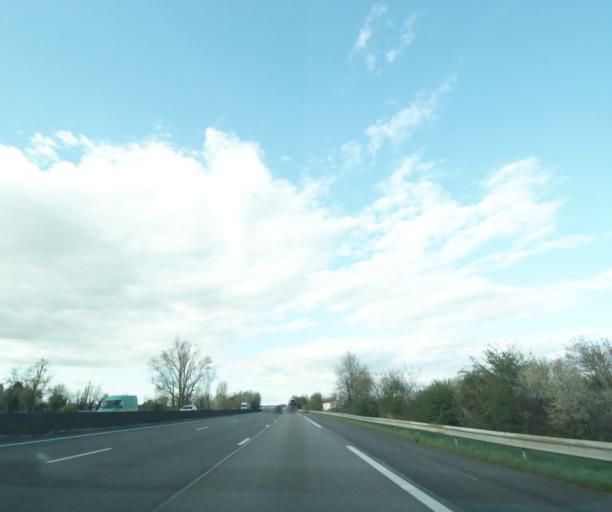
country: FR
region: Rhone-Alpes
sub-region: Departement du Rhone
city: Saint-Georges-de-Reneins
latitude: 46.0674
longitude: 4.7398
